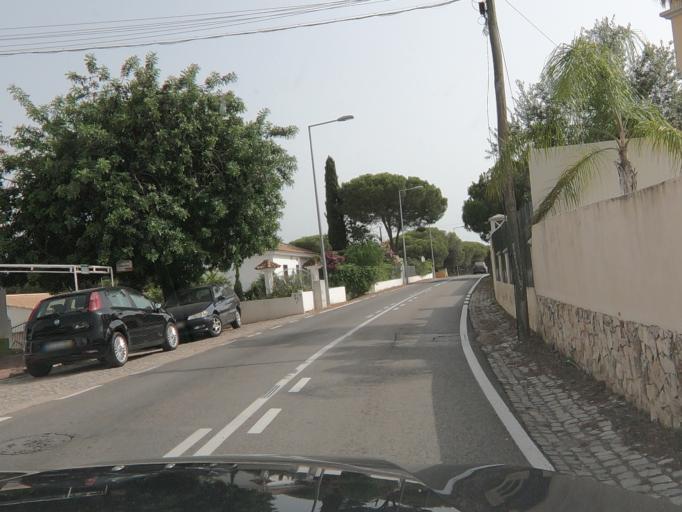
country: PT
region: Faro
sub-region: Loule
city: Quarteira
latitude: 37.0906
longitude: -8.0723
